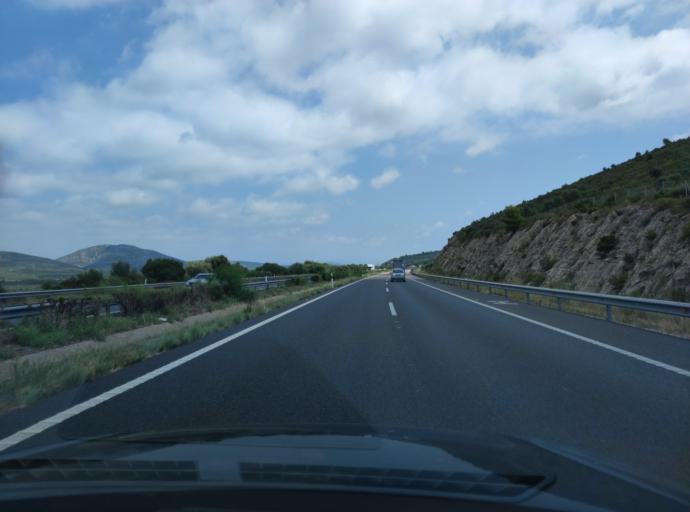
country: ES
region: Valencia
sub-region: Provincia de Castello
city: Santa Magdalena de Pulpis
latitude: 40.3725
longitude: 0.3329
